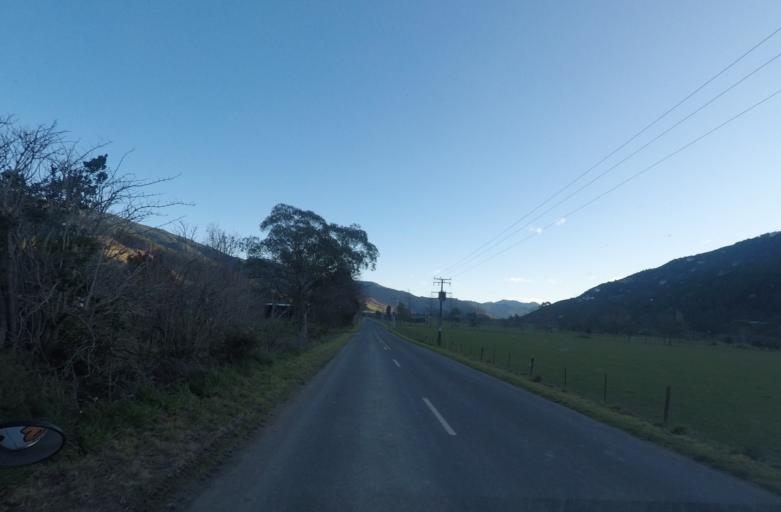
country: NZ
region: Marlborough
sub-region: Marlborough District
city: Picton
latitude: -41.2831
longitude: 173.9120
